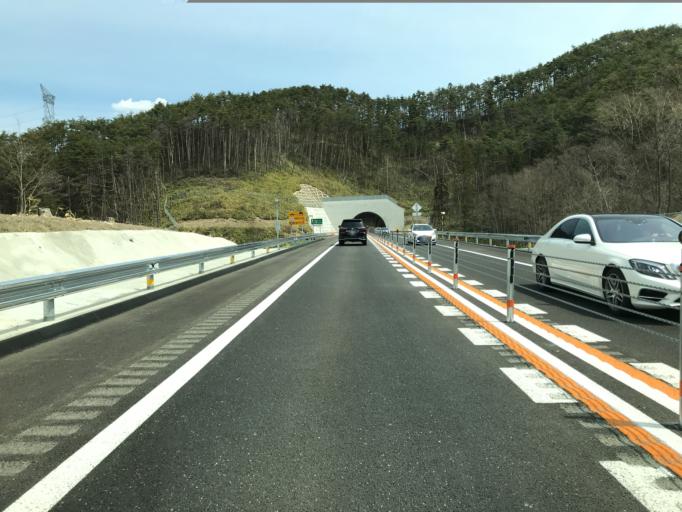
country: JP
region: Yamagata
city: Kaminoyama
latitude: 38.1006
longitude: 140.2156
